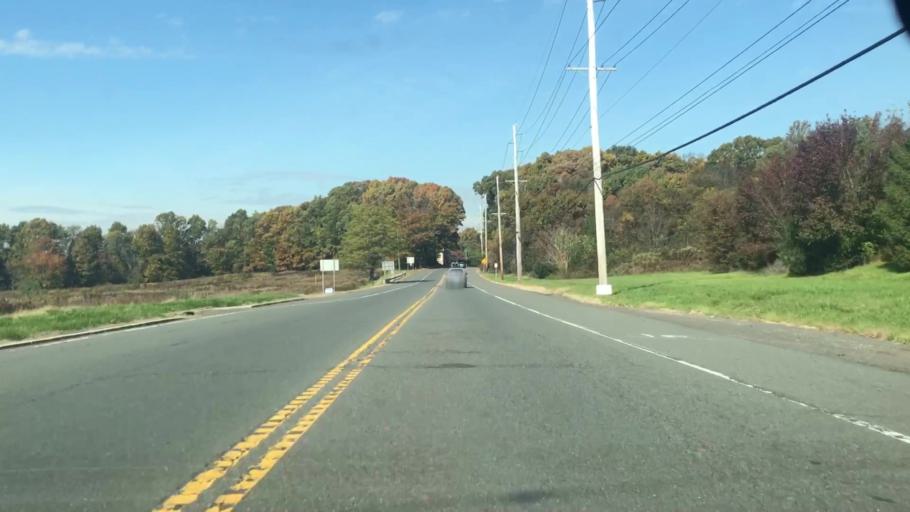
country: US
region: New Jersey
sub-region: Somerset County
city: Ten Mile Run
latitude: 40.4181
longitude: -74.6537
